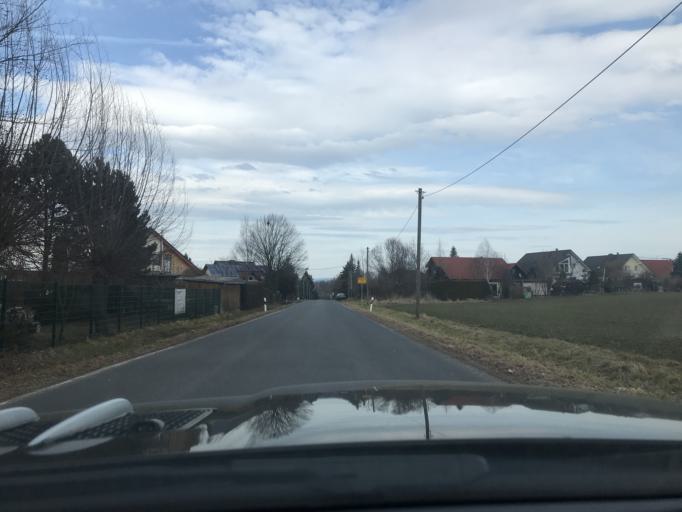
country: DE
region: Thuringia
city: Muehlhausen
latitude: 51.1978
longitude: 10.4308
